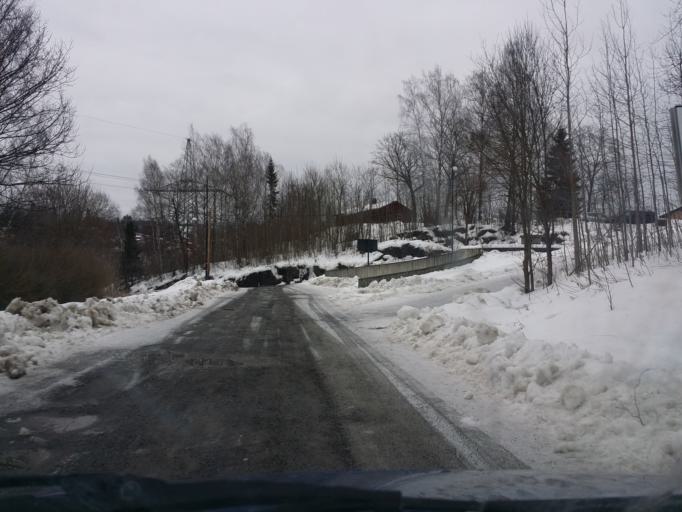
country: NO
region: Akershus
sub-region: Asker
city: Billingstad
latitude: 59.8965
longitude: 10.4930
